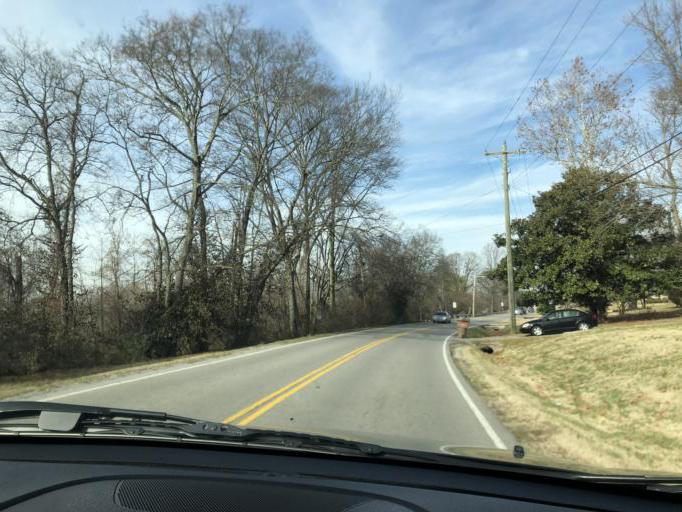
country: US
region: Tennessee
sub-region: Davidson County
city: Lakewood
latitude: 36.2100
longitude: -86.6862
